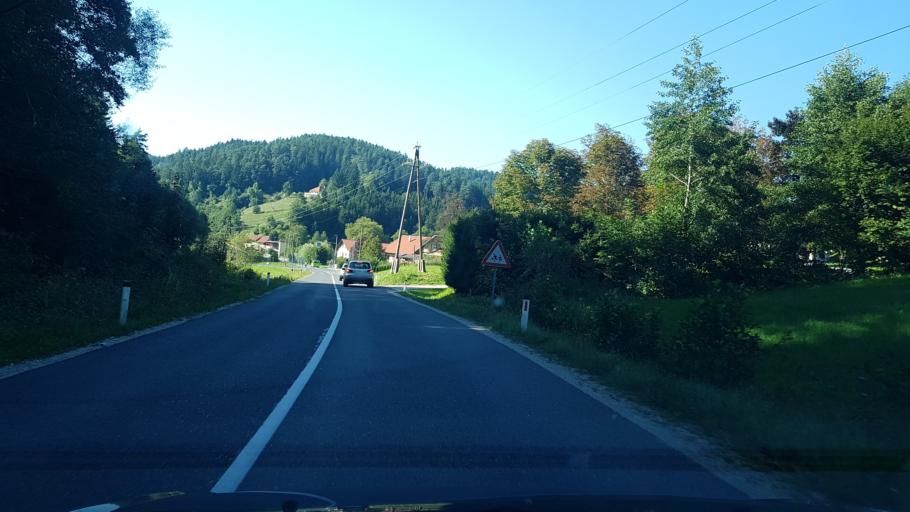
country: SI
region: Slovenj Gradec
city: Slovenj Gradec
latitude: 46.5163
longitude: 15.0435
